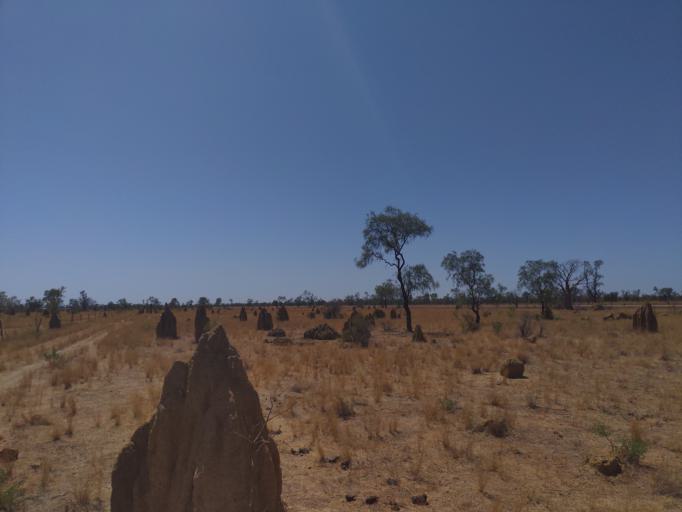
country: AU
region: Western Australia
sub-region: Derby-West Kimberley
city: Derby
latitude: -17.6714
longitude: 123.3992
